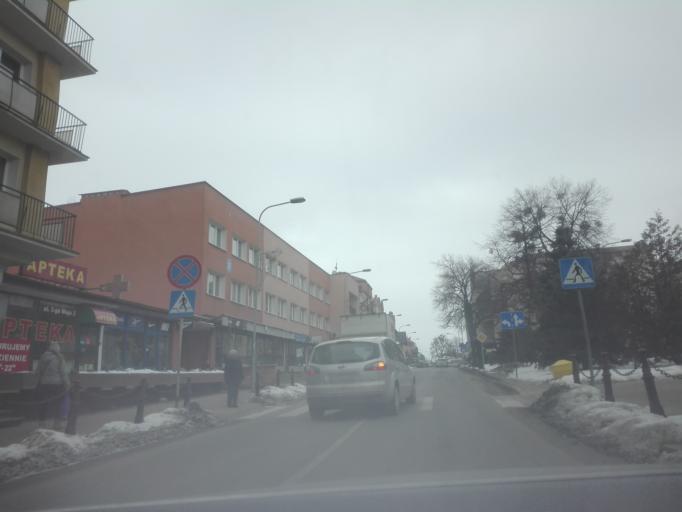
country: PL
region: Lublin Voivodeship
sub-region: Powiat hrubieszowski
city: Hrubieszow
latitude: 50.8053
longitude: 23.8910
